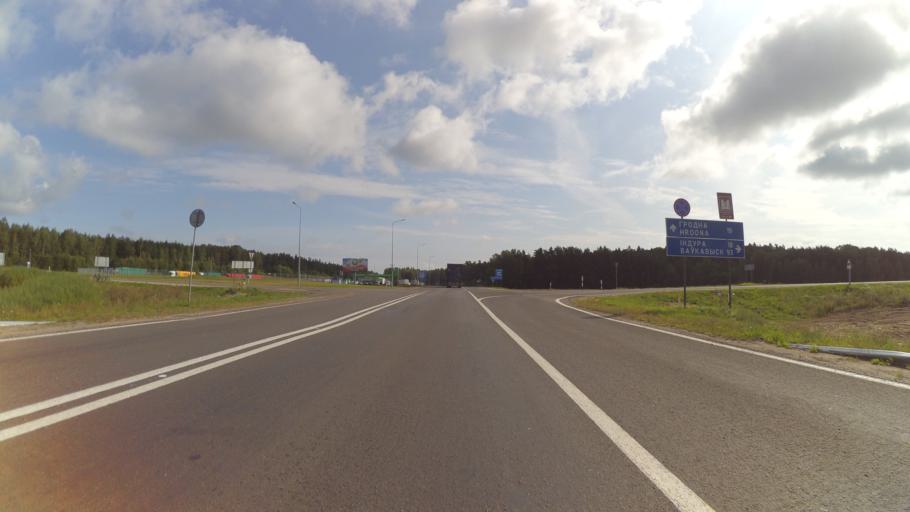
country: PL
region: Podlasie
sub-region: Powiat sokolski
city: Kuznica
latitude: 53.5300
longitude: 23.6821
